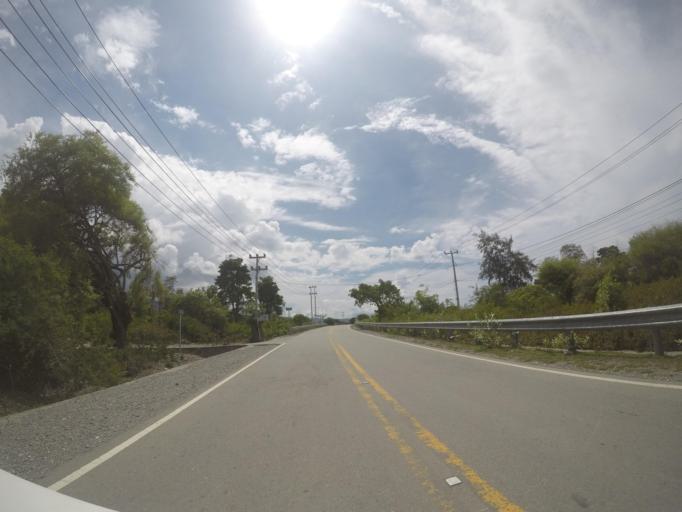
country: TL
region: Liquica
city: Liquica
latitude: -8.5840
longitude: 125.3543
